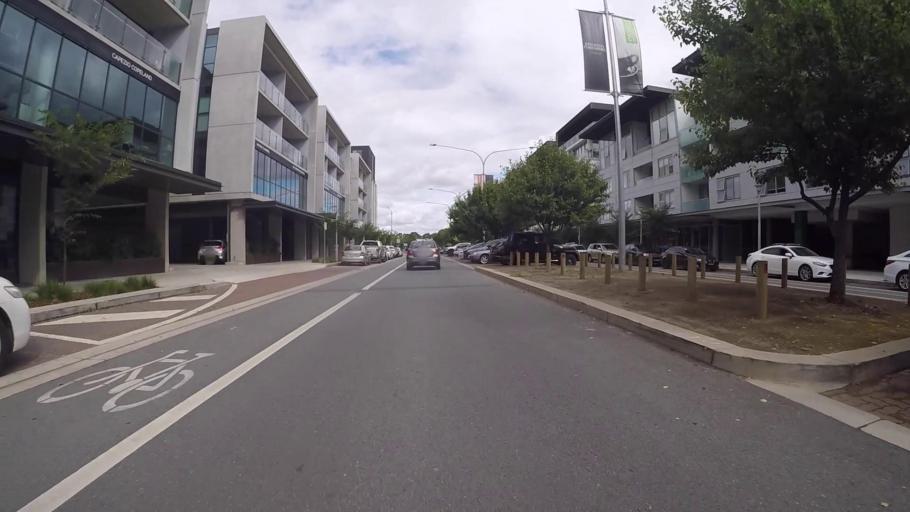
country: AU
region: Australian Capital Territory
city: Forrest
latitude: -35.3134
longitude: 149.1467
